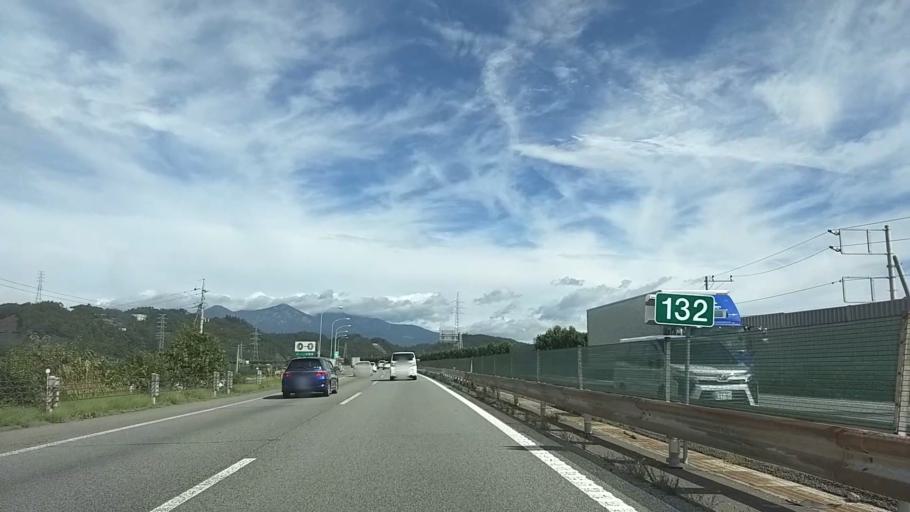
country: JP
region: Yamanashi
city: Nirasaki
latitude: 35.7778
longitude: 138.4225
